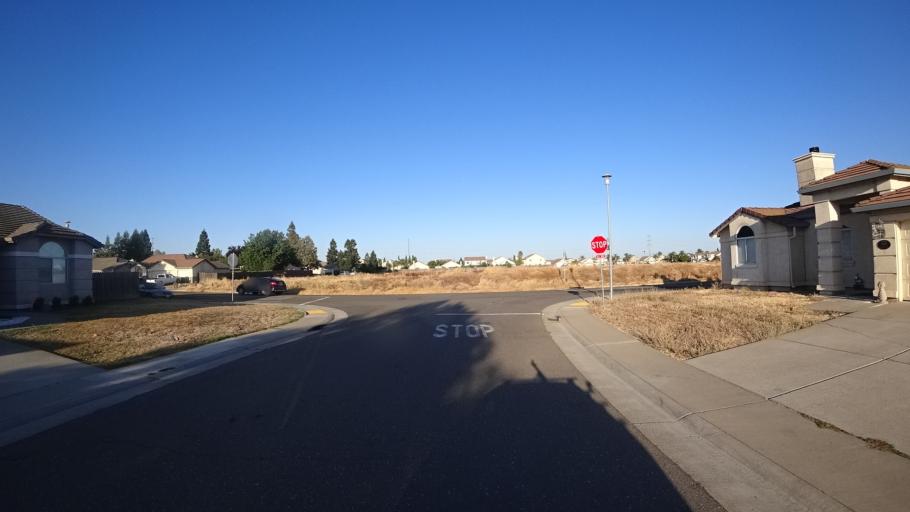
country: US
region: California
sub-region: Sacramento County
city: Laguna
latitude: 38.4273
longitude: -121.4522
